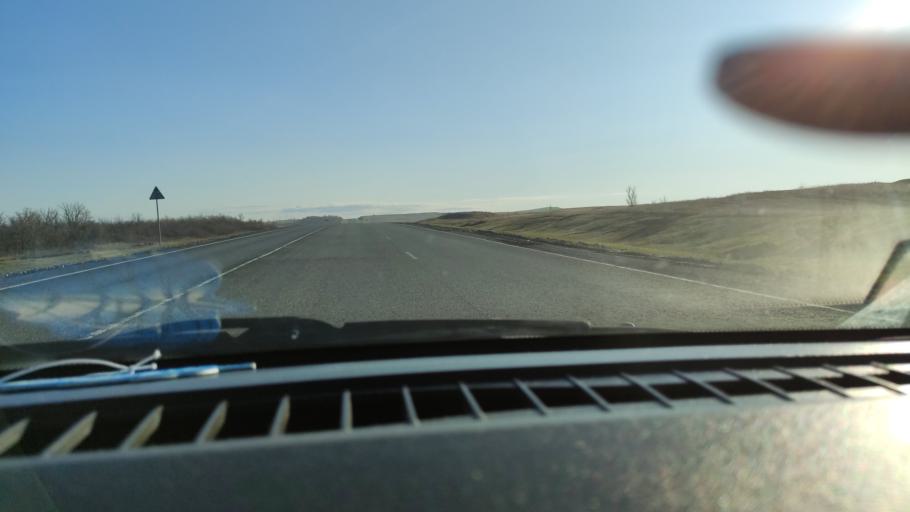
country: RU
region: Saratov
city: Alekseyevka
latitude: 52.2081
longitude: 47.8756
